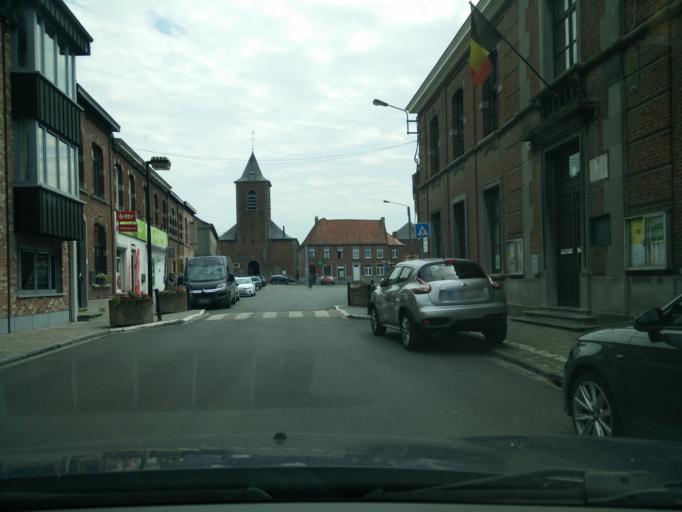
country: BE
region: Wallonia
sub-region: Province du Hainaut
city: Soignies
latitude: 50.5540
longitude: 4.0999
